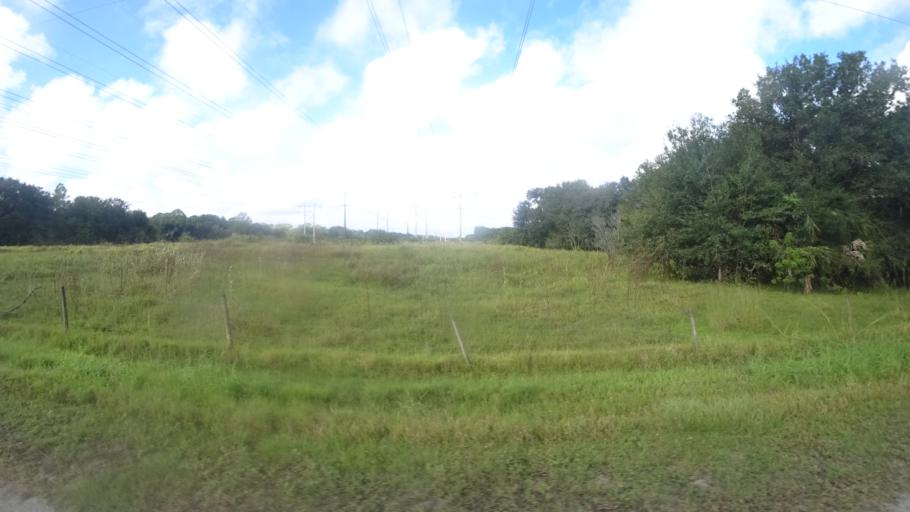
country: US
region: Florida
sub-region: Hillsborough County
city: Sun City Center
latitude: 27.6020
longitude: -82.3637
